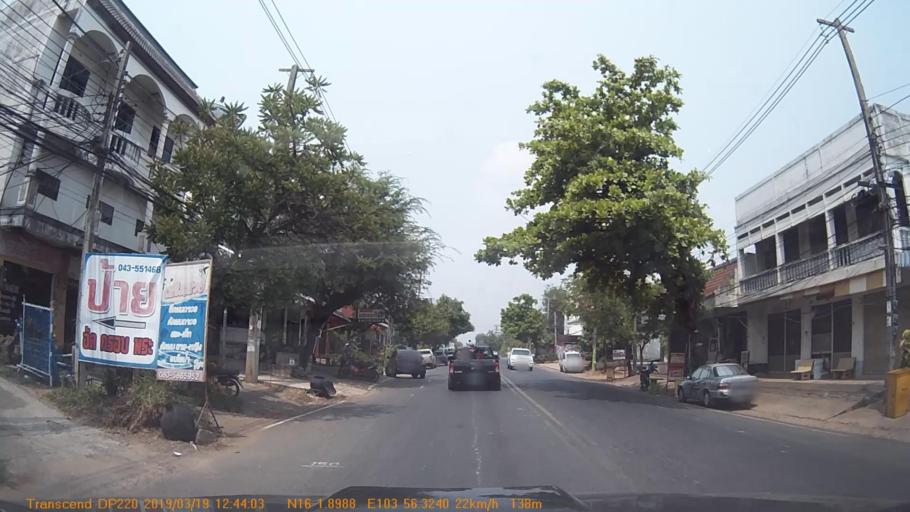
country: TH
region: Roi Et
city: Selaphum
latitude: 16.0317
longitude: 103.9387
